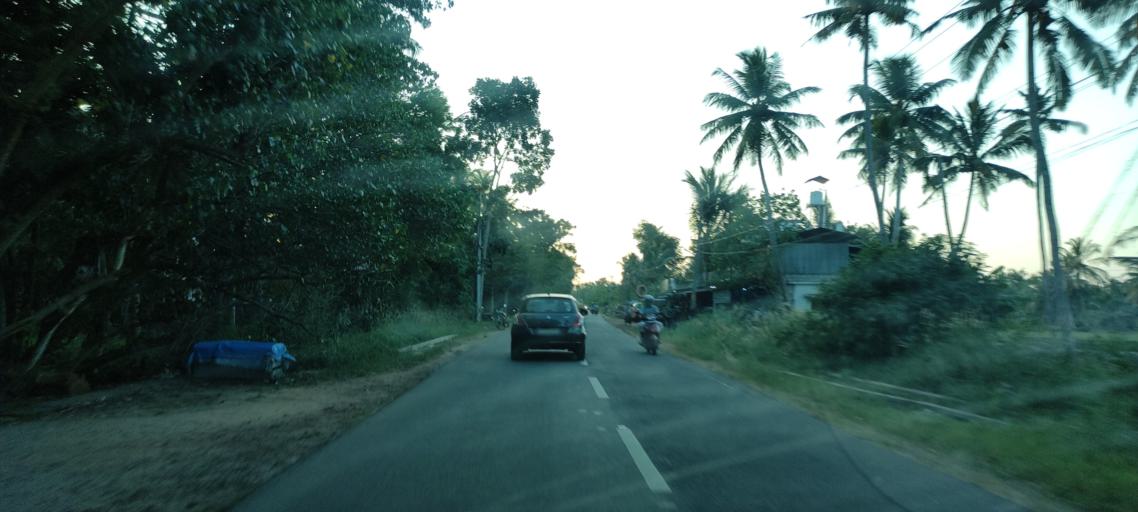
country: IN
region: Kerala
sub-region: Alappuzha
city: Kayankulam
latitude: 9.2577
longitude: 76.4234
